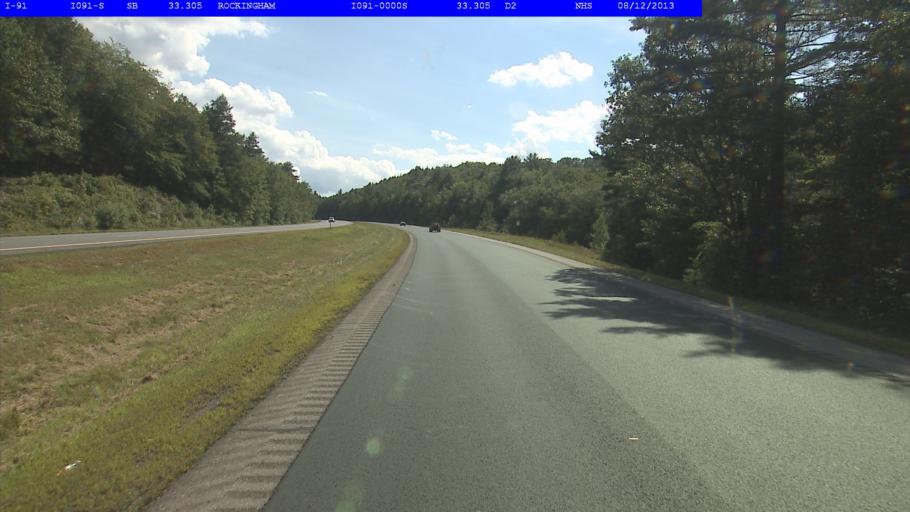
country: US
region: Vermont
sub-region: Windham County
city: Bellows Falls
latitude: 43.1542
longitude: -72.4736
